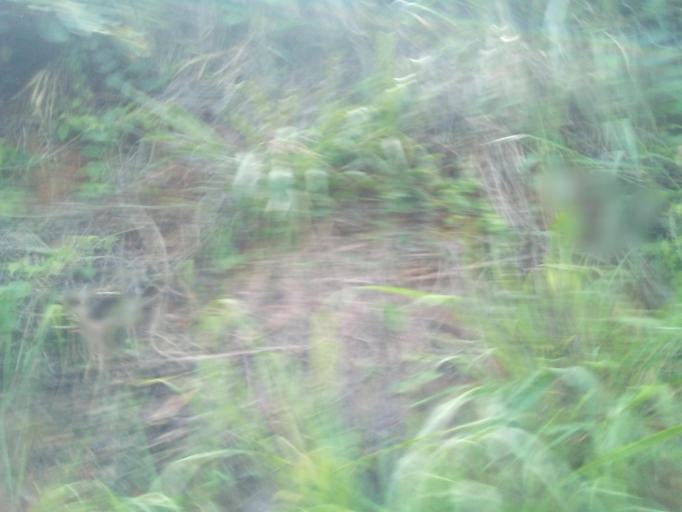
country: BR
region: Espirito Santo
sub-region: Ibiracu
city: Ibiracu
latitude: -19.8431
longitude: -40.3533
